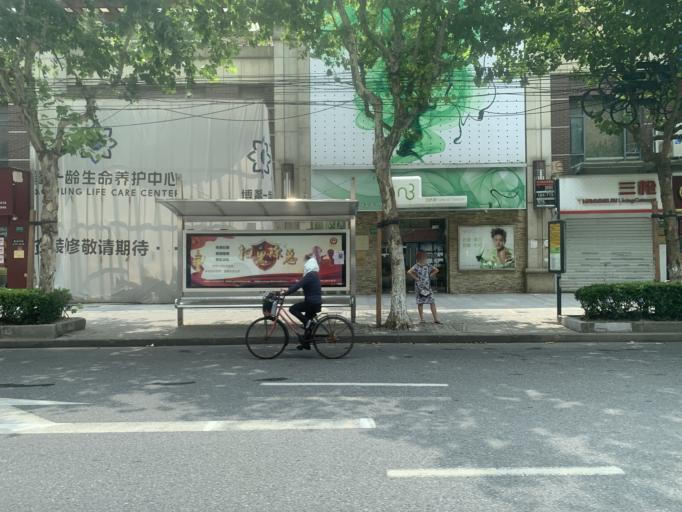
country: CN
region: Shanghai Shi
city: Huamu
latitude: 31.1816
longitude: 121.5183
